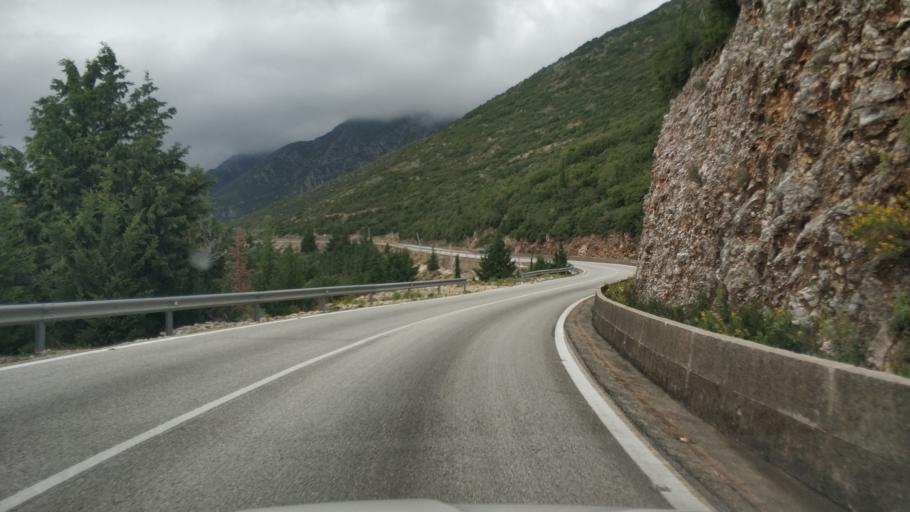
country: AL
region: Vlore
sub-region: Rrethi i Vlores
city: Vranisht
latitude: 40.1416
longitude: 19.6871
